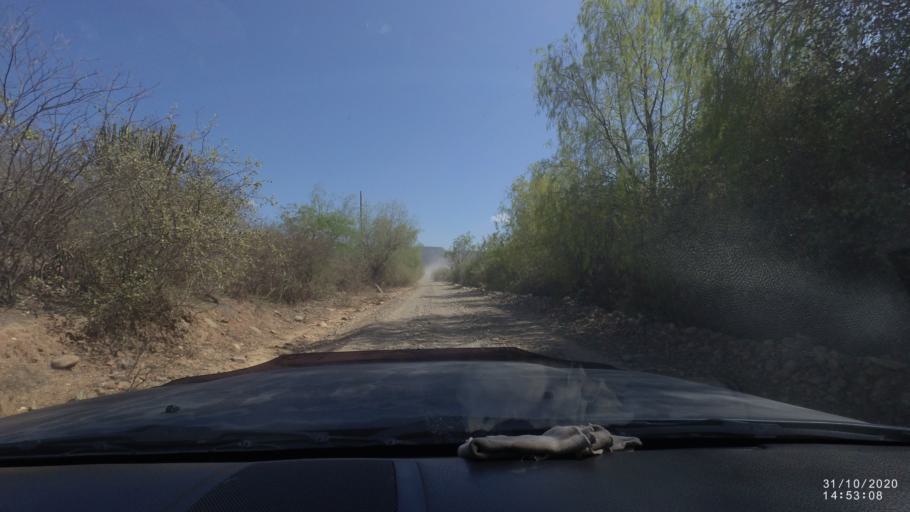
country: BO
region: Cochabamba
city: Aiquile
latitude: -18.2169
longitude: -64.8571
